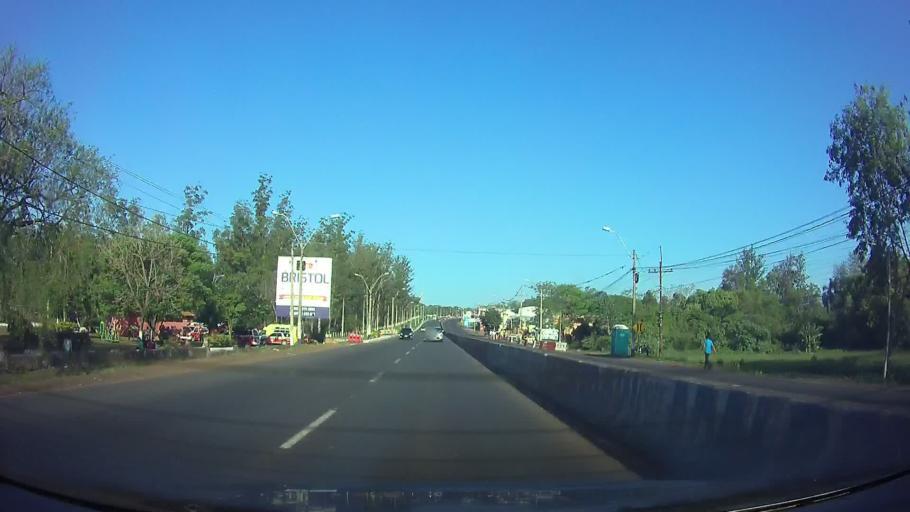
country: PY
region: Central
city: Capiata
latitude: -25.3584
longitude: -57.4366
